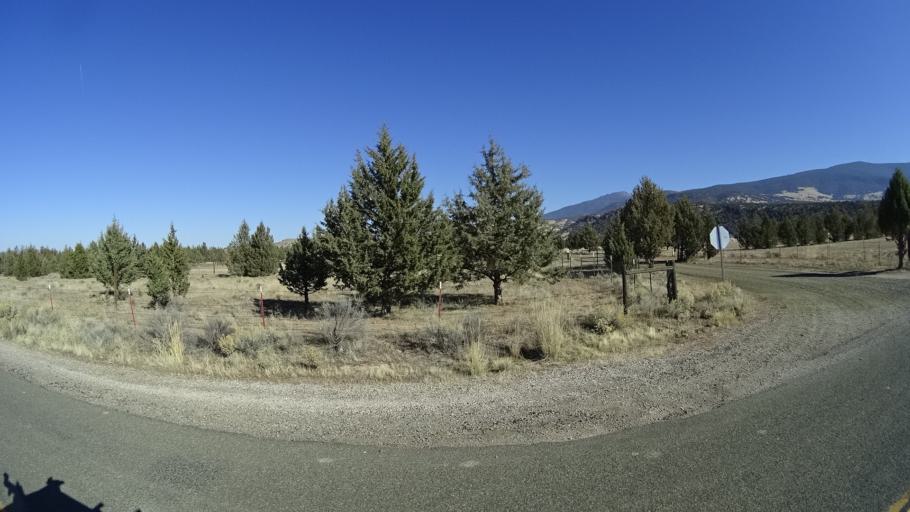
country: US
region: California
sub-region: Siskiyou County
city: Montague
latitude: 41.6430
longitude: -122.3497
